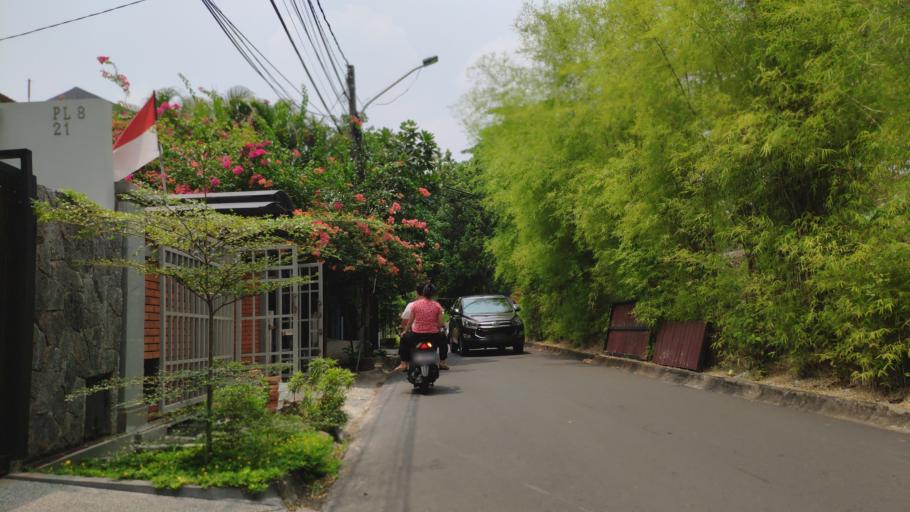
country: ID
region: Banten
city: South Tangerang
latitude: -6.2703
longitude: 106.7768
